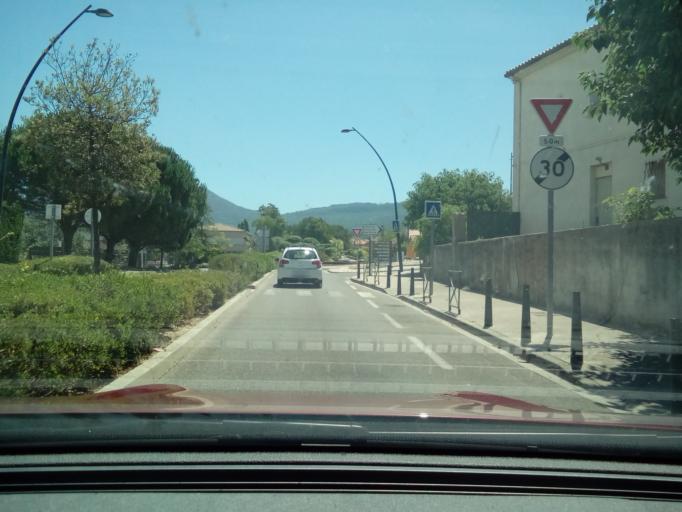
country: FR
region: Provence-Alpes-Cote d'Azur
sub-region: Departement des Bouches-du-Rhone
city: Trets
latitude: 43.4501
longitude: 5.6765
